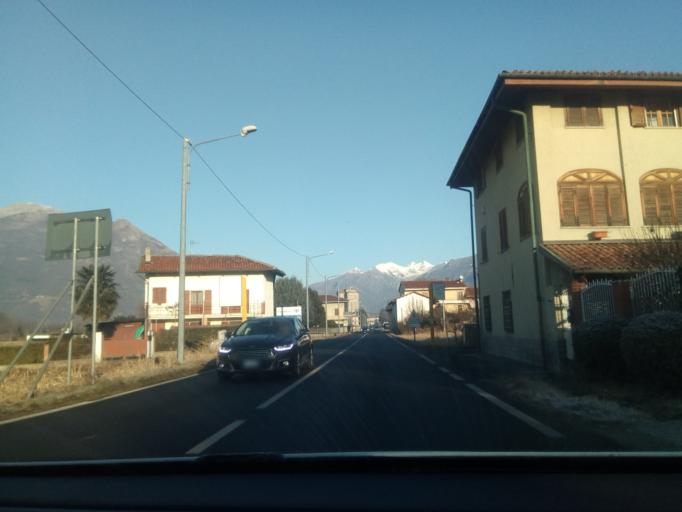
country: IT
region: Piedmont
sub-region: Provincia di Torino
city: Montalto Dora
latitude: 45.4780
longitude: 7.8656
